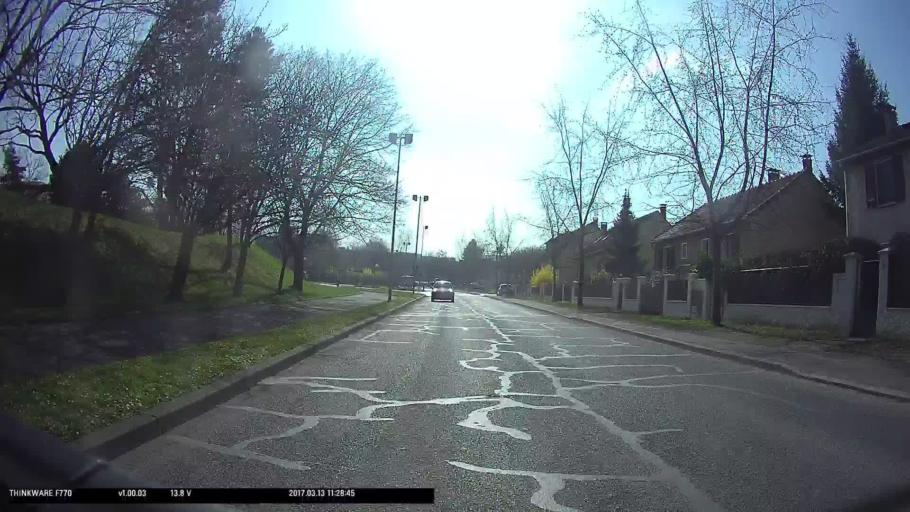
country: FR
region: Ile-de-France
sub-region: Departement de Seine-Saint-Denis
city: Noisy-le-Grand
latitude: 48.8442
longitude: 2.5719
